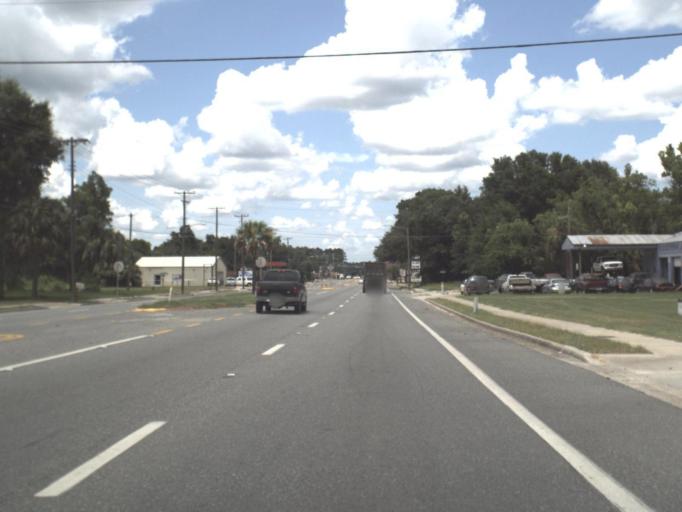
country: US
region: Florida
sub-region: Taylor County
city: Perry
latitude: 30.1068
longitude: -83.5892
